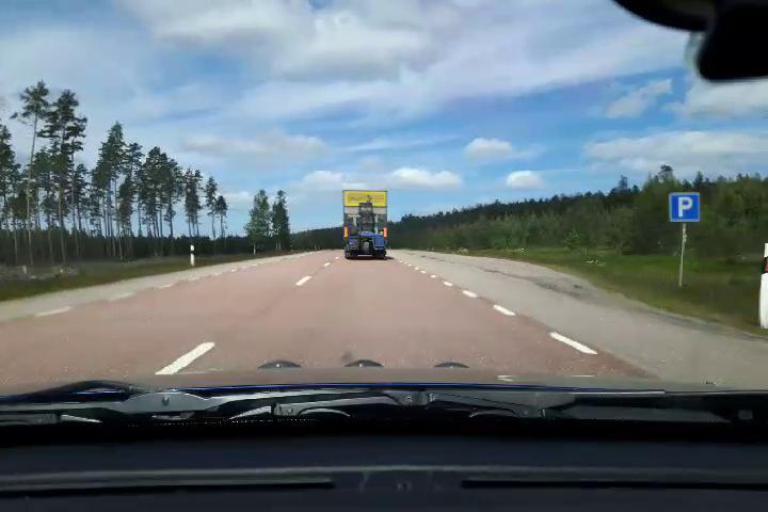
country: SE
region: Uppsala
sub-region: Osthammars Kommun
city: Bjorklinge
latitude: 60.1638
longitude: 17.4915
